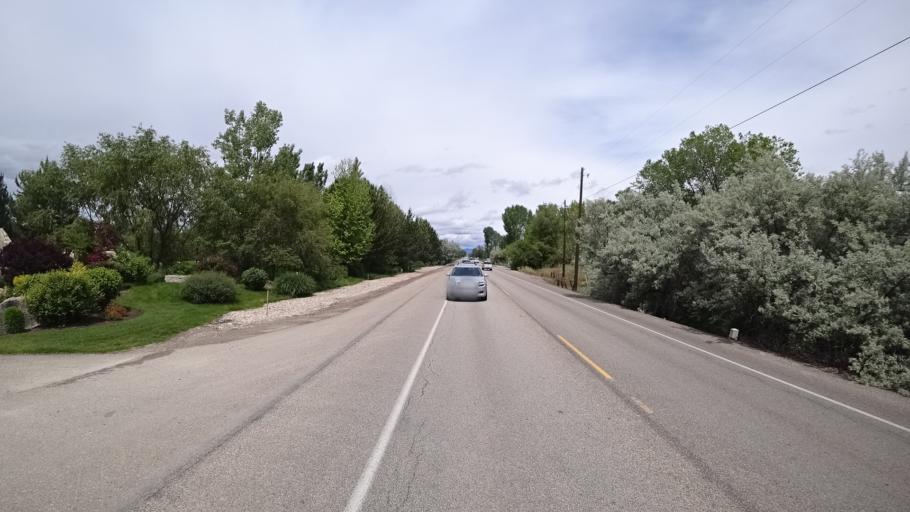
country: US
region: Idaho
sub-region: Ada County
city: Eagle
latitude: 43.6788
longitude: -116.4137
